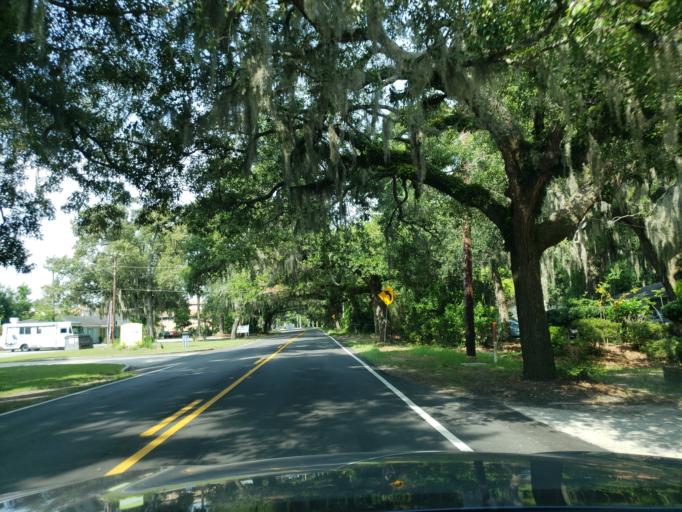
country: US
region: Georgia
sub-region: Chatham County
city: Wilmington Island
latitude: 32.0193
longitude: -80.9748
